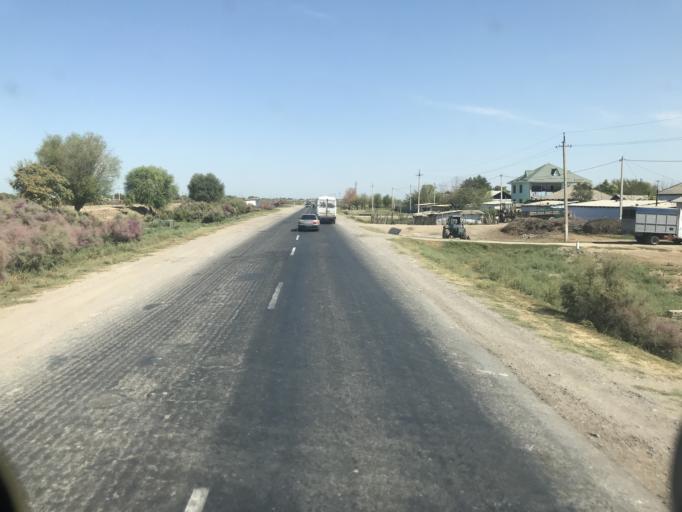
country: KZ
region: Ongtustik Qazaqstan
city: Myrzakent
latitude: 40.7313
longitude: 68.5365
